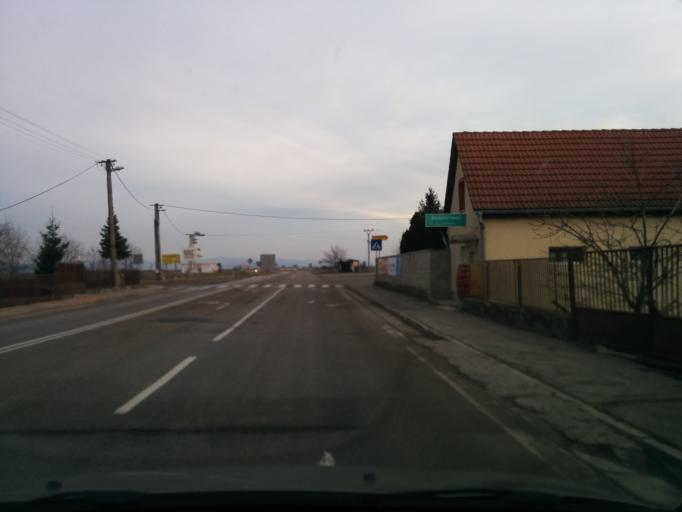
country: SK
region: Trnavsky
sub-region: Okres Trnava
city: Piestany
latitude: 48.6598
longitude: 17.8417
